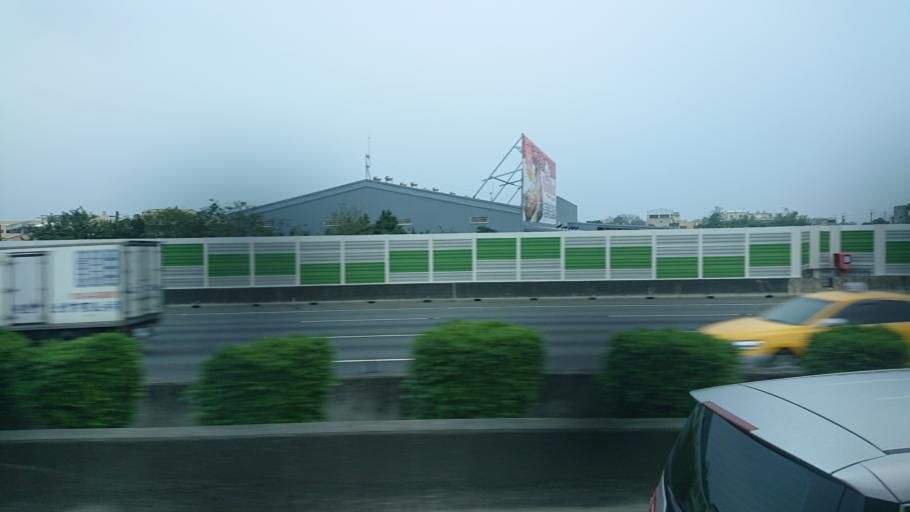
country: TW
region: Taiwan
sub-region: Nantou
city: Nantou
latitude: 23.8833
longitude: 120.4916
